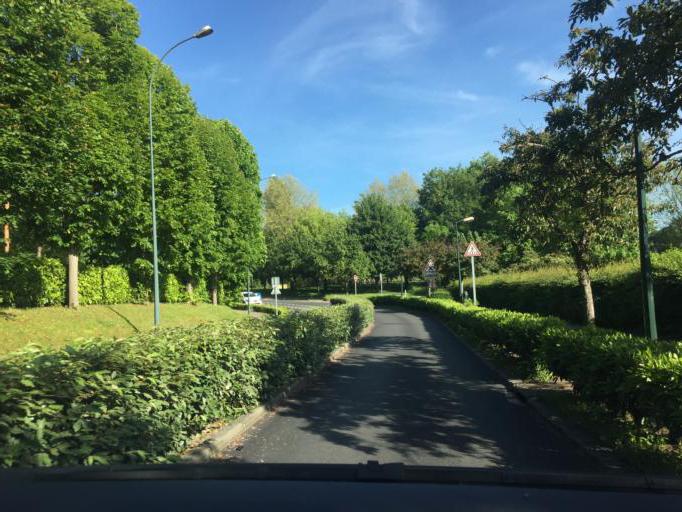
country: FR
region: Ile-de-France
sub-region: Departement de l'Essonne
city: Villiers-le-Bacle
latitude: 48.7063
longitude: 2.1254
